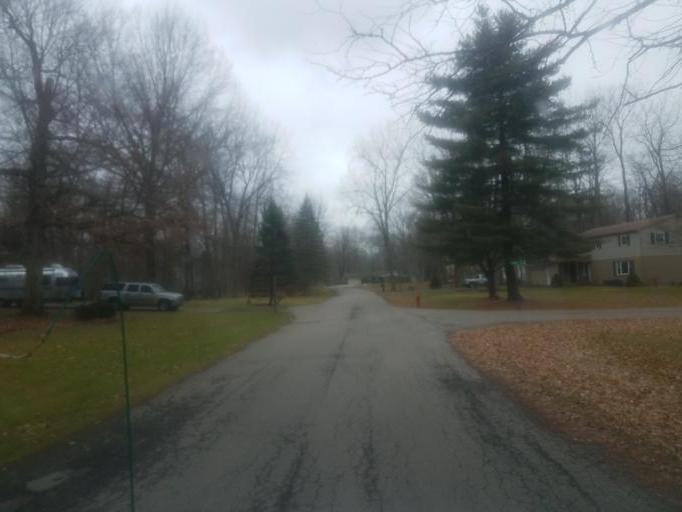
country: US
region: Ohio
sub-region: Crawford County
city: Galion
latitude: 40.7452
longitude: -82.8076
